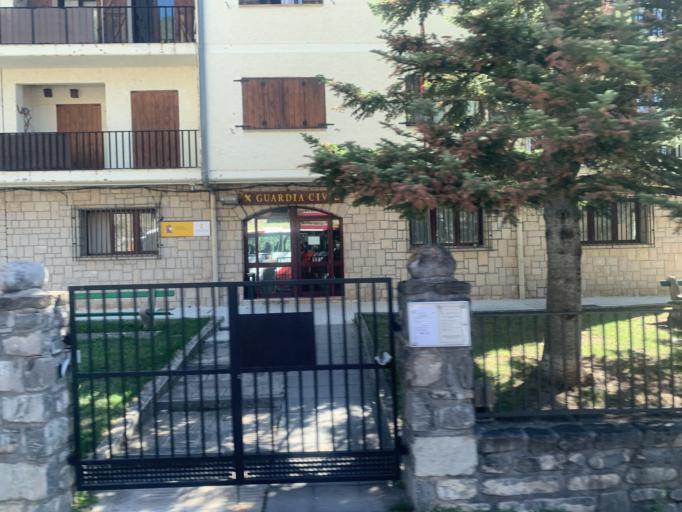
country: ES
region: Aragon
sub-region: Provincia de Huesca
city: Broto
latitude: 42.6298
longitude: -0.1123
